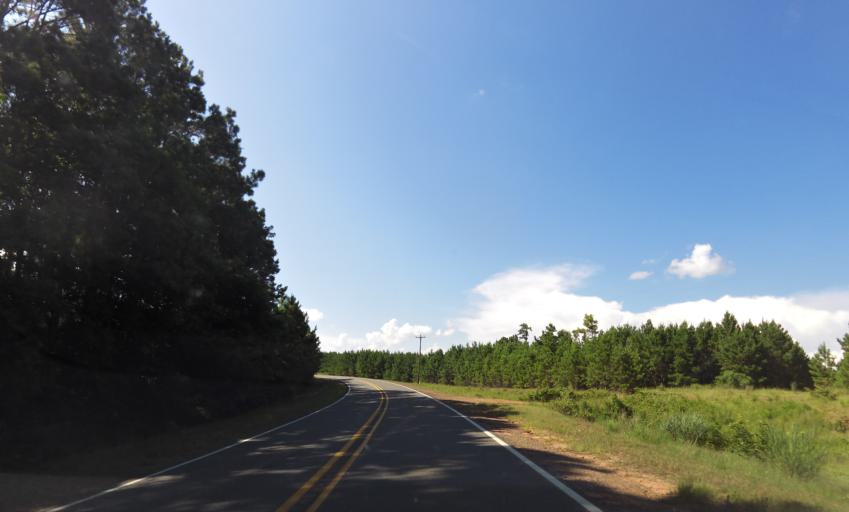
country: US
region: Louisiana
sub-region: Sabine Parish
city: Many
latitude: 31.4231
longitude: -93.5801
